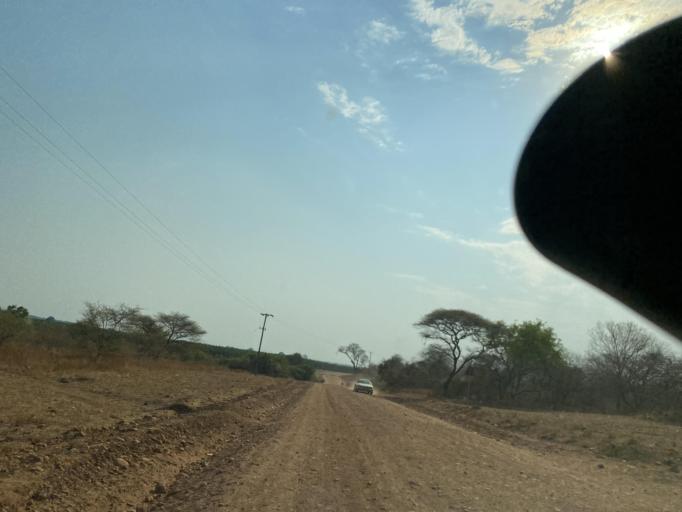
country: ZW
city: Chirundu
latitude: -15.9298
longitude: 28.9657
